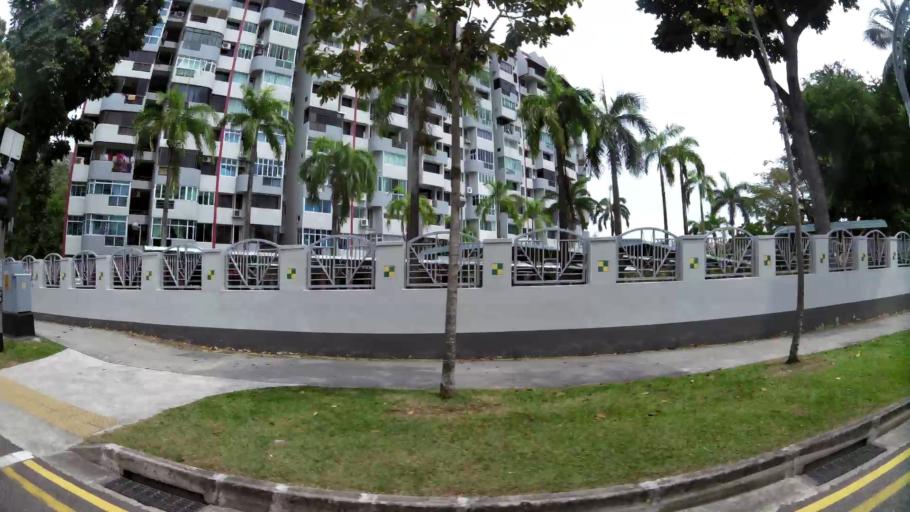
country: MY
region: Johor
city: Johor Bahru
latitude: 1.3403
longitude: 103.7161
